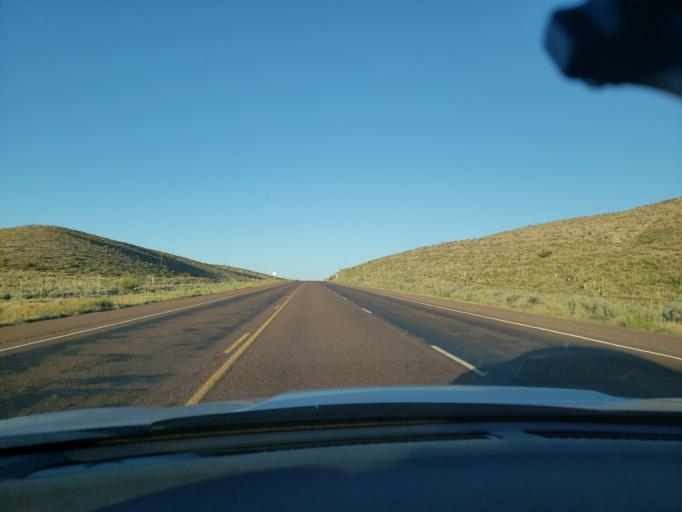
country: US
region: Texas
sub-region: El Paso County
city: Homestead Meadows South
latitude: 31.8271
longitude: -105.8956
